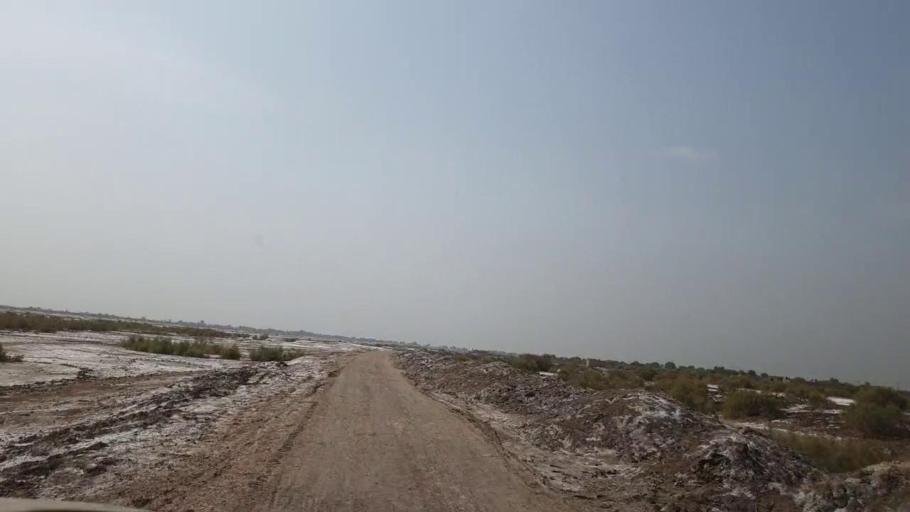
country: PK
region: Sindh
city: Dokri
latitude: 27.4209
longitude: 68.2054
